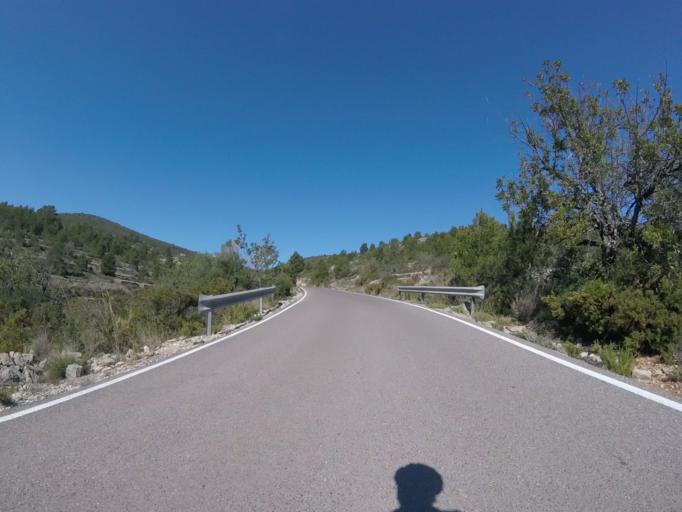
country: ES
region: Valencia
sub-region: Provincia de Castello
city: Santa Magdalena de Pulpis
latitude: 40.3834
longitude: 0.2614
